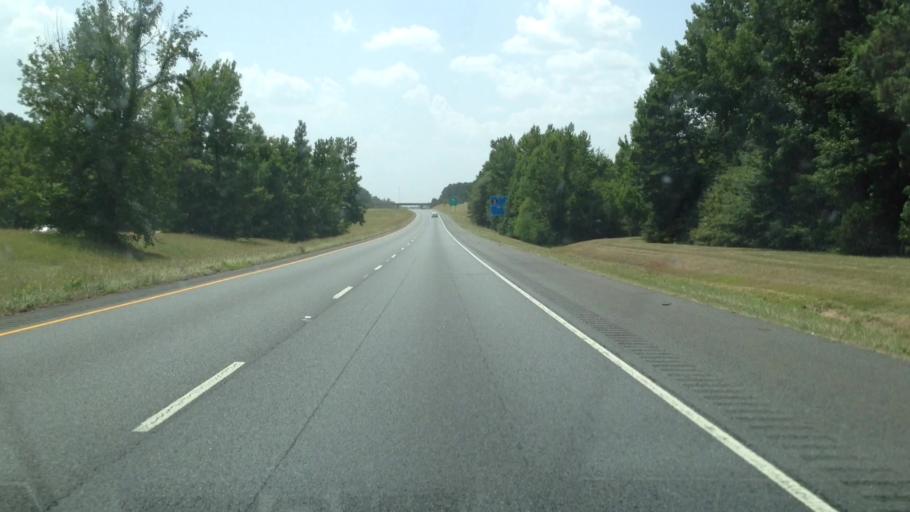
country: US
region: Louisiana
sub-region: Lincoln Parish
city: Grambling
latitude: 32.5462
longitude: -92.7575
